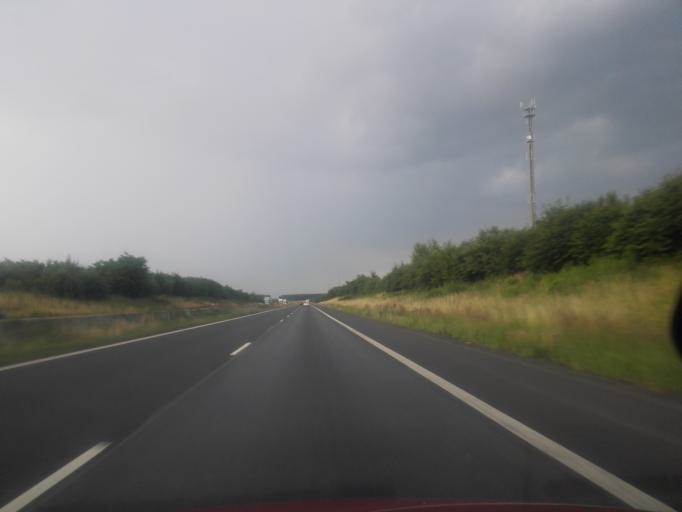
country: PL
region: Silesian Voivodeship
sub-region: Powiat czestochowski
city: Borowno
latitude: 50.9659
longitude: 19.2601
